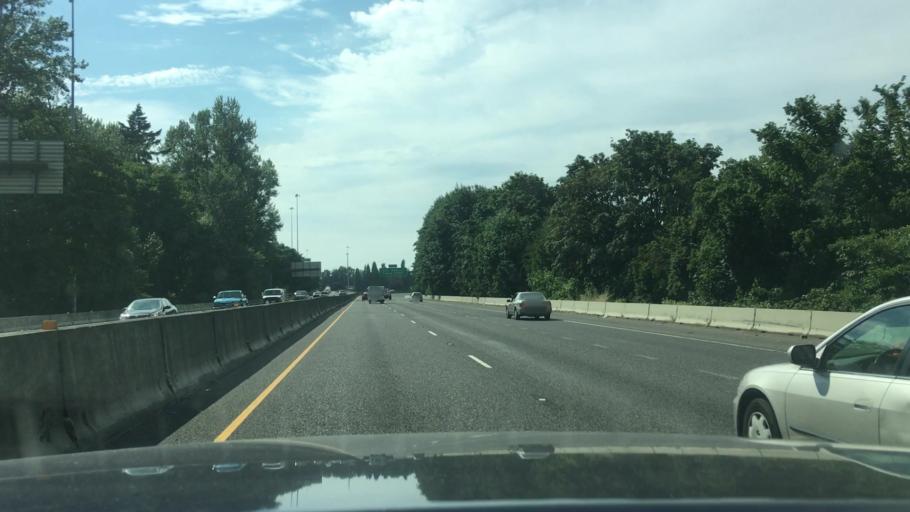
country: US
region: Oregon
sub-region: Lane County
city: Eugene
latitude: 44.0622
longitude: -123.0909
